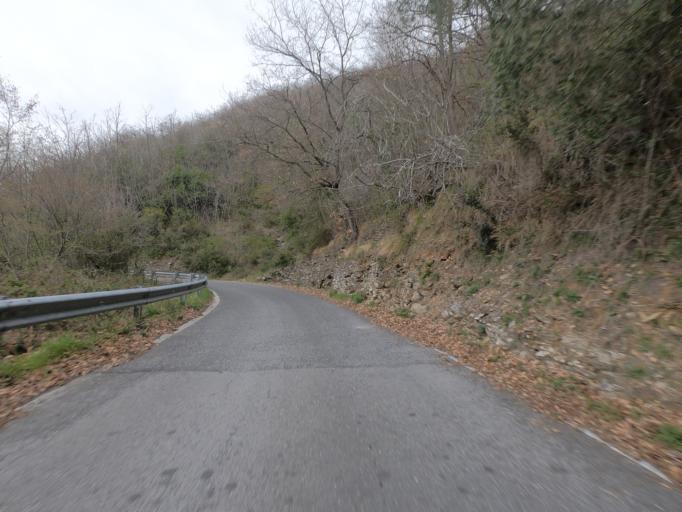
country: IT
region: Liguria
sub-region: Provincia di Savona
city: Testico
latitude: 44.0283
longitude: 8.0150
